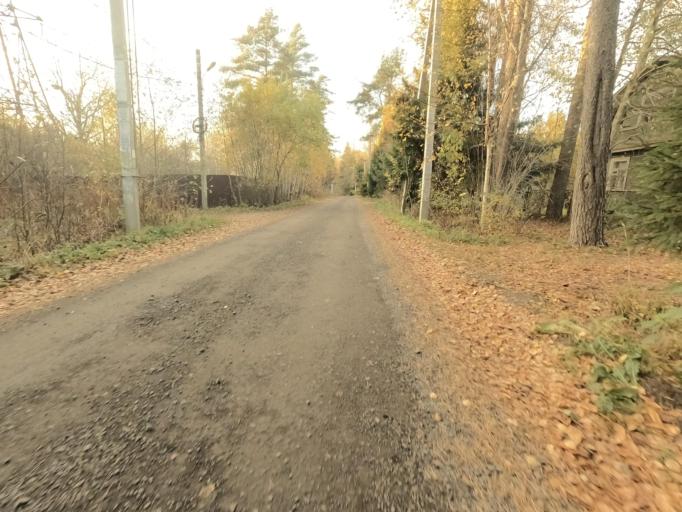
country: RU
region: St.-Petersburg
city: Beloostrov
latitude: 60.1713
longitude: 29.9837
